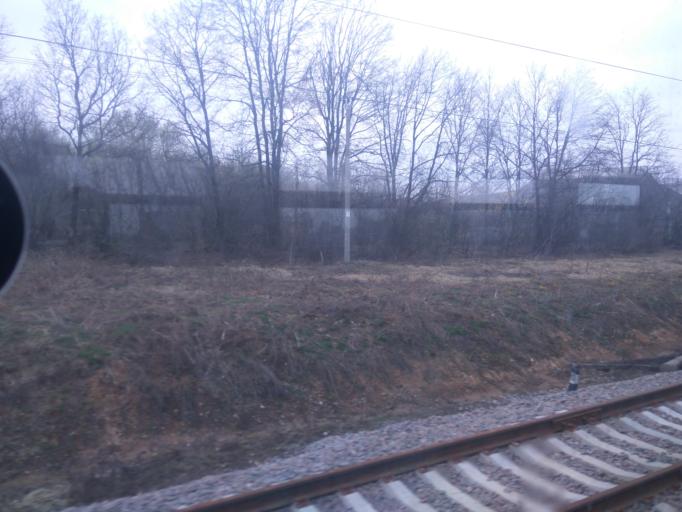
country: RU
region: Moskovskaya
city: Sergiyev Posad
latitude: 56.3429
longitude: 38.1211
